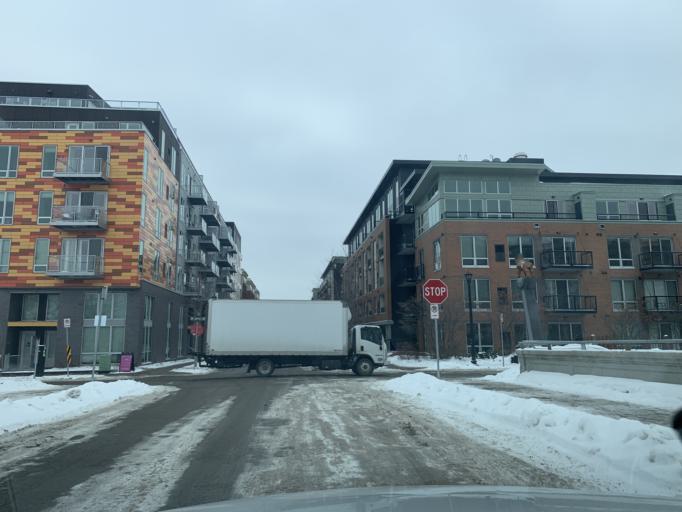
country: US
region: Minnesota
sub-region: Hennepin County
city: Minneapolis
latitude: 44.9503
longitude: -93.2894
